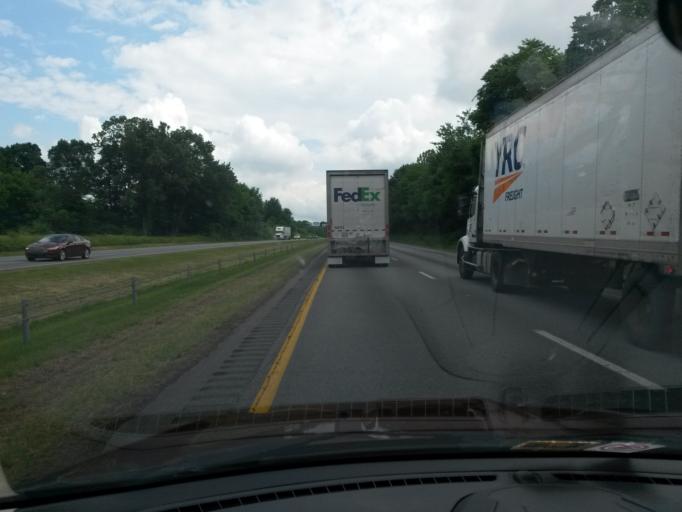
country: US
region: North Carolina
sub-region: Yadkin County
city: Jonesville
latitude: 36.2204
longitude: -80.8121
